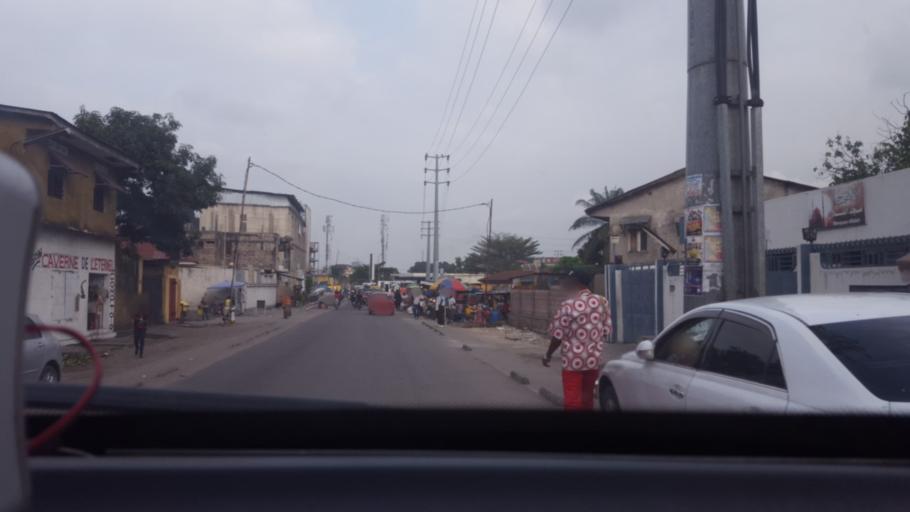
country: CD
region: Kinshasa
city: Kinshasa
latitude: -4.3346
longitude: 15.3162
